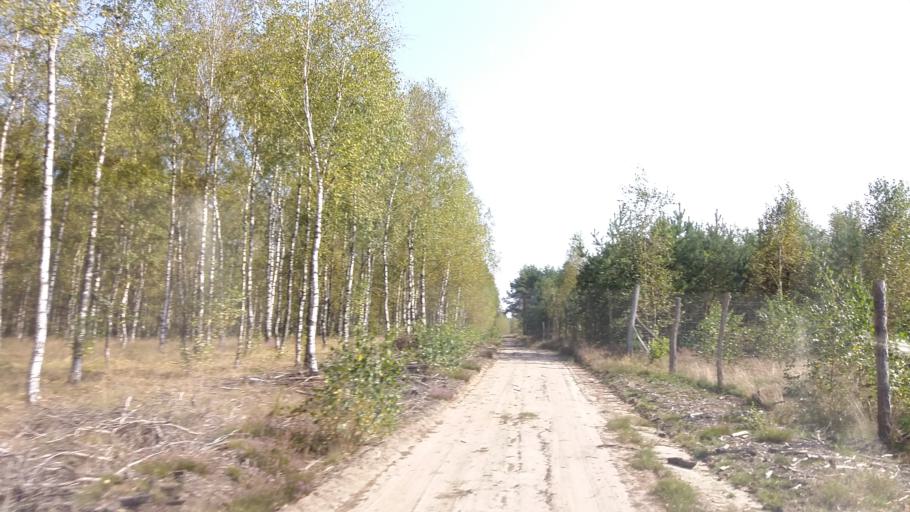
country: PL
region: West Pomeranian Voivodeship
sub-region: Powiat drawski
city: Kalisz Pomorski
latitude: 53.1371
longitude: 15.9389
